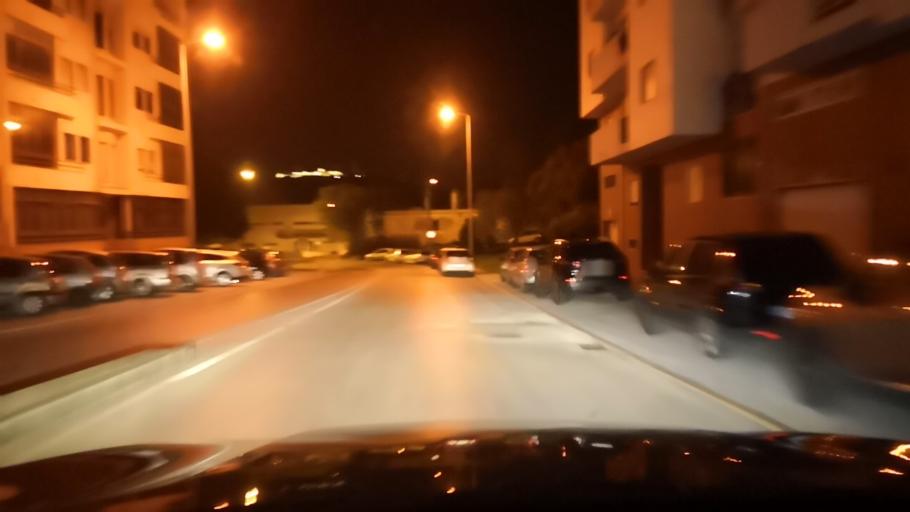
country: PT
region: Setubal
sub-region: Setubal
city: Setubal
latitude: 38.5427
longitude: -8.8784
